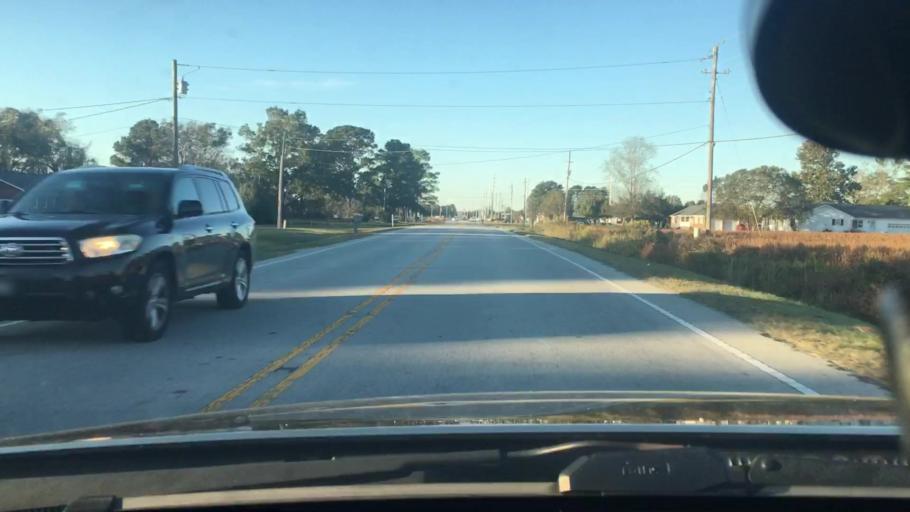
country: US
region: North Carolina
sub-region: Pitt County
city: Windsor
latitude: 35.5268
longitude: -77.3193
